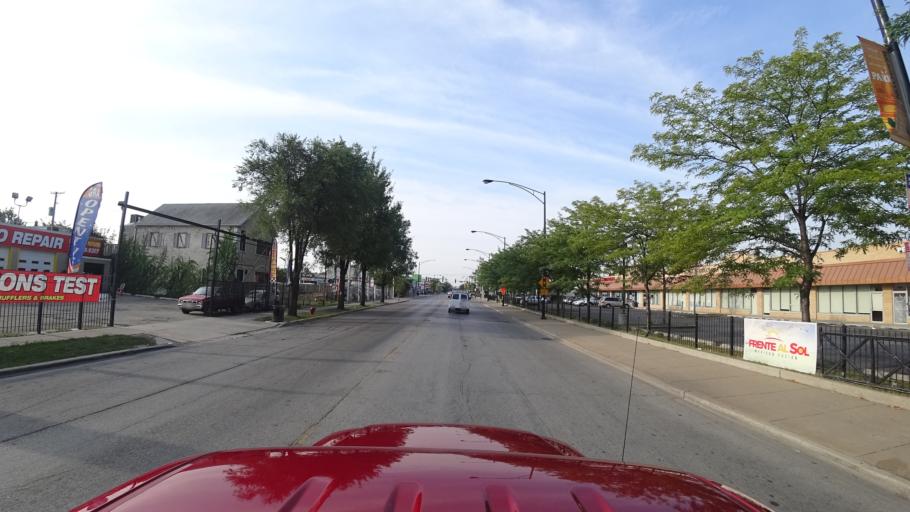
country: US
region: Illinois
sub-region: Cook County
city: Cicero
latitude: 41.8093
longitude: -87.7041
